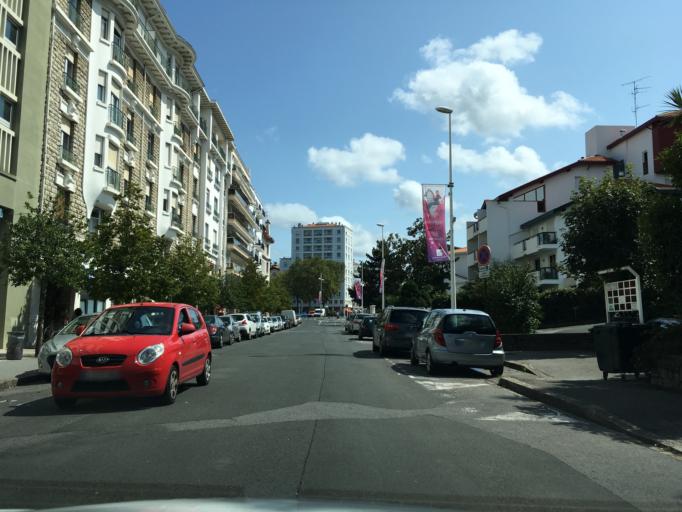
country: FR
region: Aquitaine
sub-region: Departement des Pyrenees-Atlantiques
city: Bayonne
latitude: 43.4937
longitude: -1.4817
